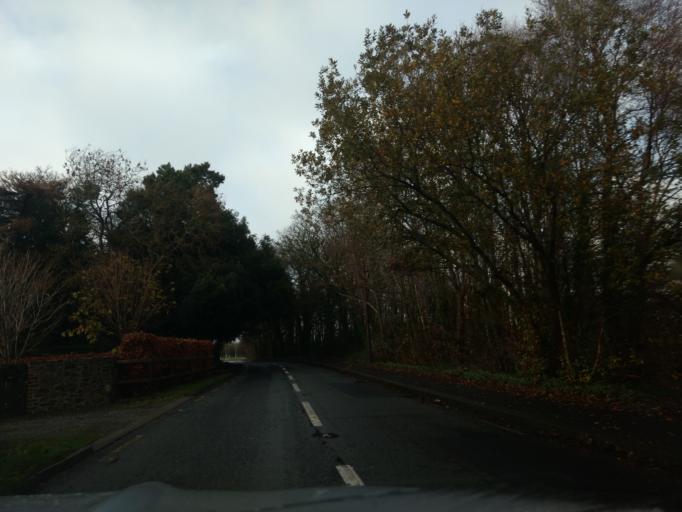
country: IE
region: Leinster
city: Kinsealy-Drinan
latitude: 53.4623
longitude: -6.1960
